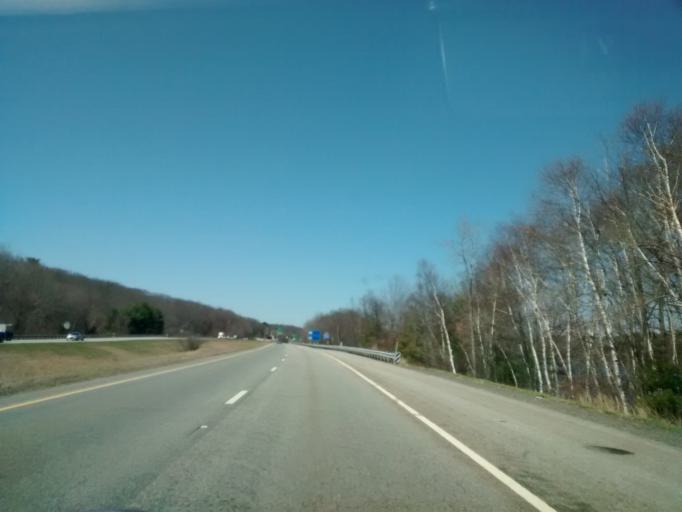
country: US
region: Massachusetts
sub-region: Worcester County
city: Auburn
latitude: 42.1739
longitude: -71.8440
